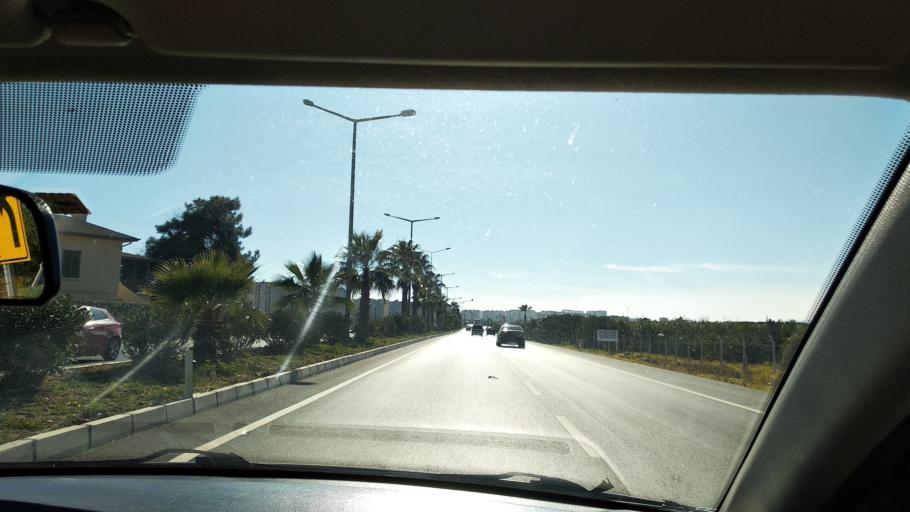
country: TR
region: Mersin
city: Tomuk
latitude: 36.6652
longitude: 34.3984
